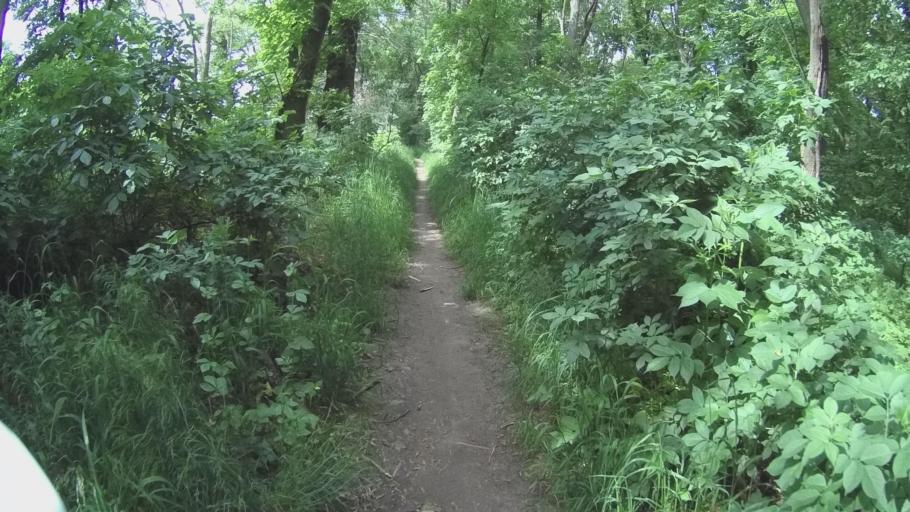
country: CZ
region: Central Bohemia
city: Zdiby
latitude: 50.1761
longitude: 14.4669
